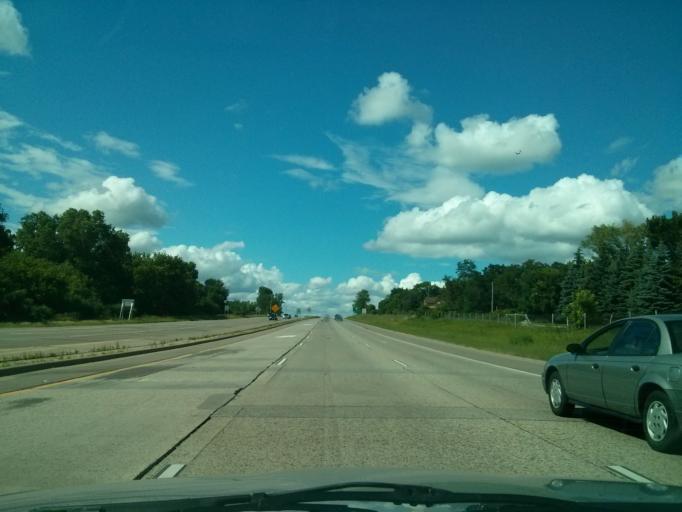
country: US
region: Minnesota
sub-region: Dakota County
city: Apple Valley
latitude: 44.7511
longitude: -93.2177
